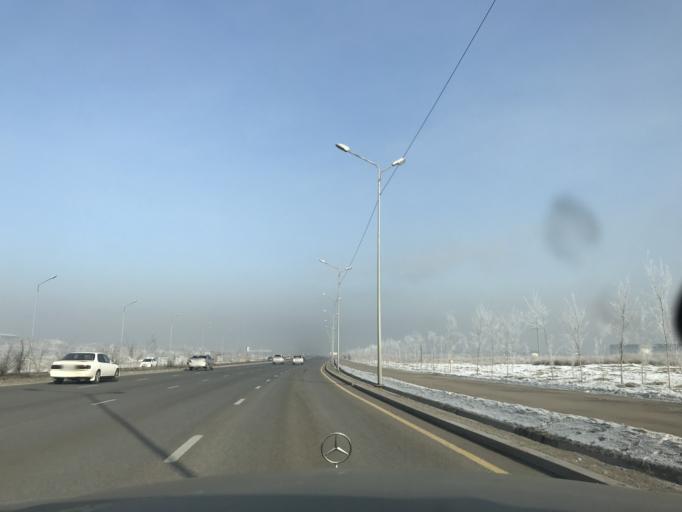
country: KZ
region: Almaty Oblysy
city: Burunday
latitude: 43.3176
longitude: 76.8339
